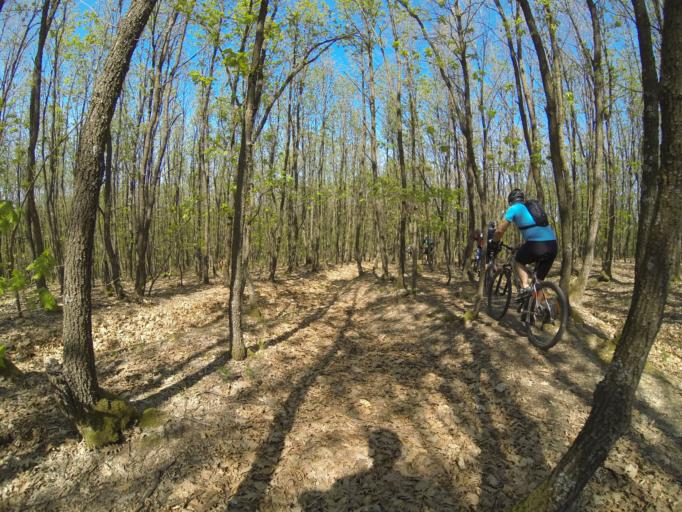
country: RO
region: Gorj
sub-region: Comuna Crusetu
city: Crusetu
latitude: 44.6122
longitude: 23.6496
